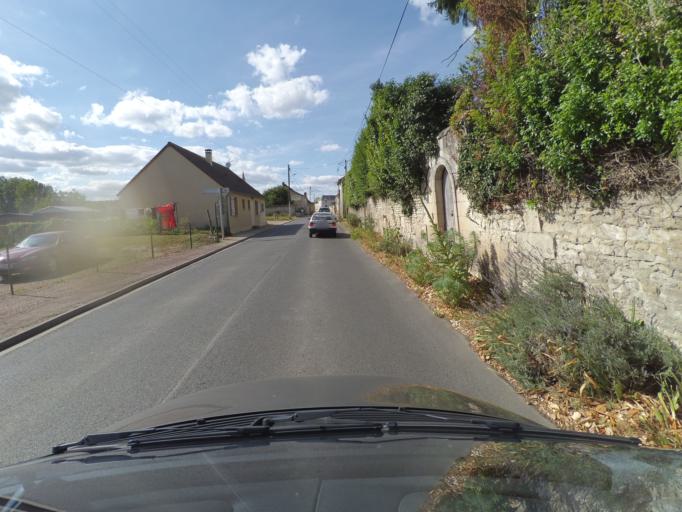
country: FR
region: Poitou-Charentes
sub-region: Departement de la Vienne
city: Saint-Gervais-les-Trois-Clochers
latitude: 46.9470
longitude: 0.4156
